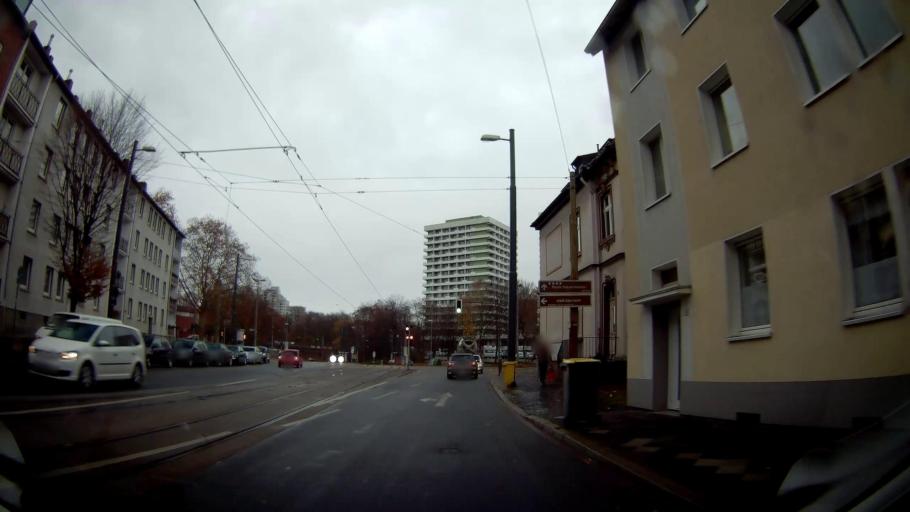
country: DE
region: North Rhine-Westphalia
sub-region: Regierungsbezirk Munster
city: Gelsenkirchen
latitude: 51.5090
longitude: 7.0841
